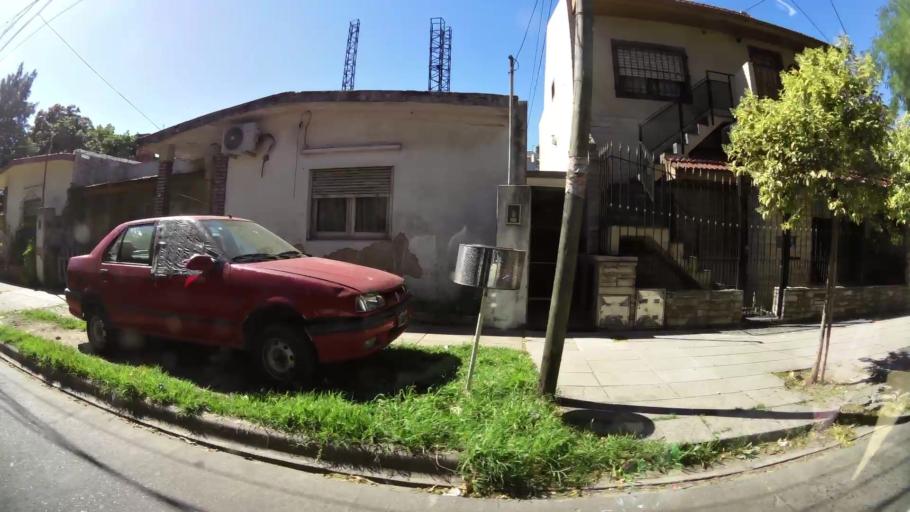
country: AR
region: Buenos Aires
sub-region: Partido de Vicente Lopez
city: Olivos
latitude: -34.5266
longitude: -58.5097
